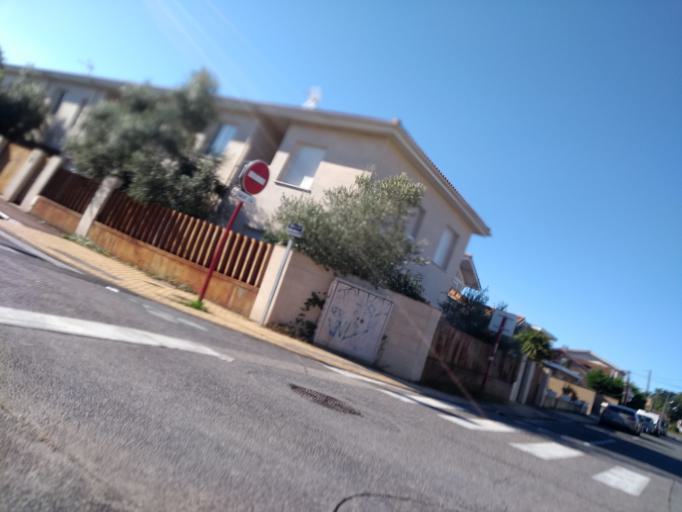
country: FR
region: Aquitaine
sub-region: Departement de la Gironde
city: Talence
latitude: 44.8057
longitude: -0.6144
